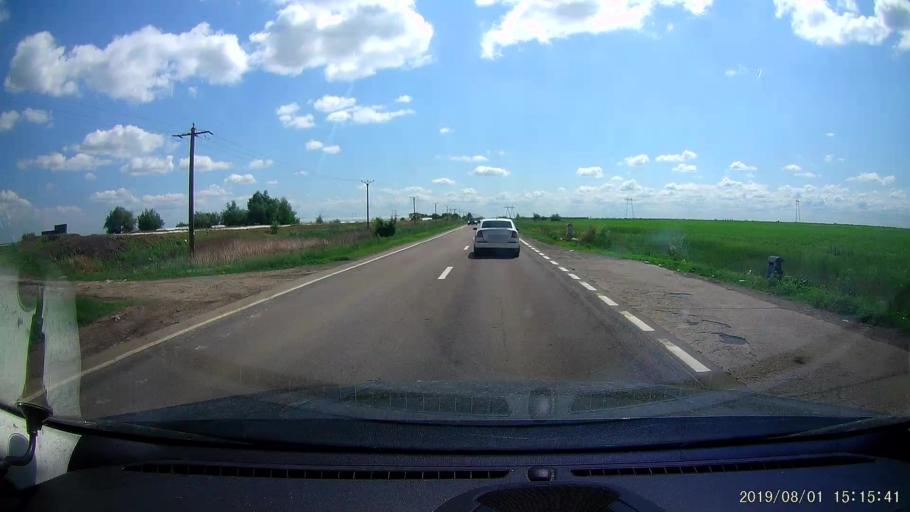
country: RO
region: Braila
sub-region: Comuna Tichilesti
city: Tichilesti
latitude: 45.1602
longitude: 27.8646
